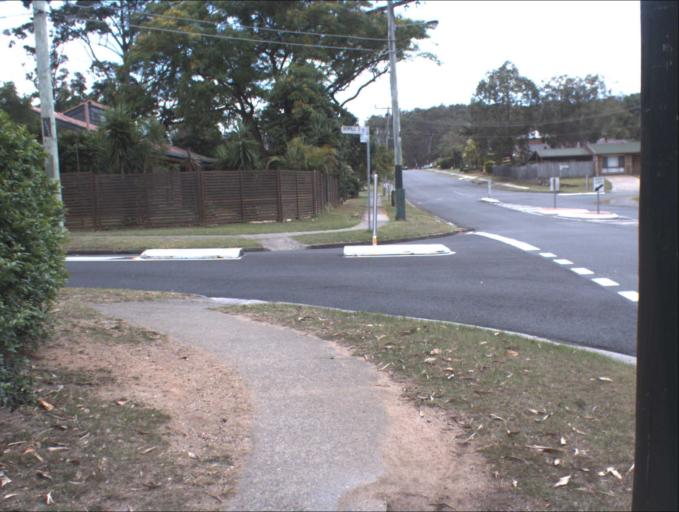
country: AU
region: Queensland
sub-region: Logan
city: Slacks Creek
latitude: -27.6318
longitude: 153.1389
